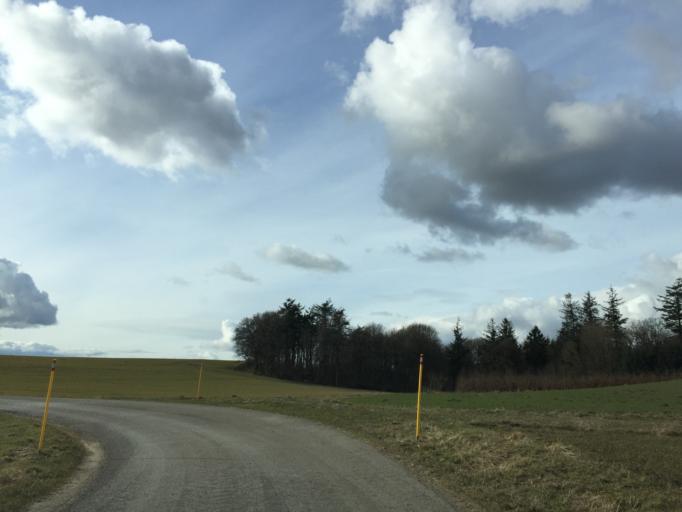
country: DK
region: Central Jutland
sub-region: Favrskov Kommune
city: Hammel
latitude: 56.2012
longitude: 9.7988
